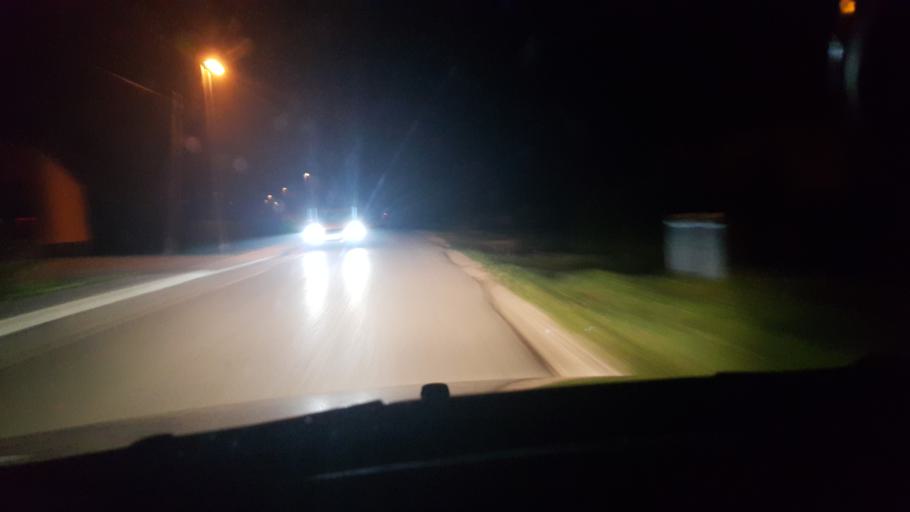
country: SI
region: Makole
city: Makole
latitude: 46.3558
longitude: 15.6594
